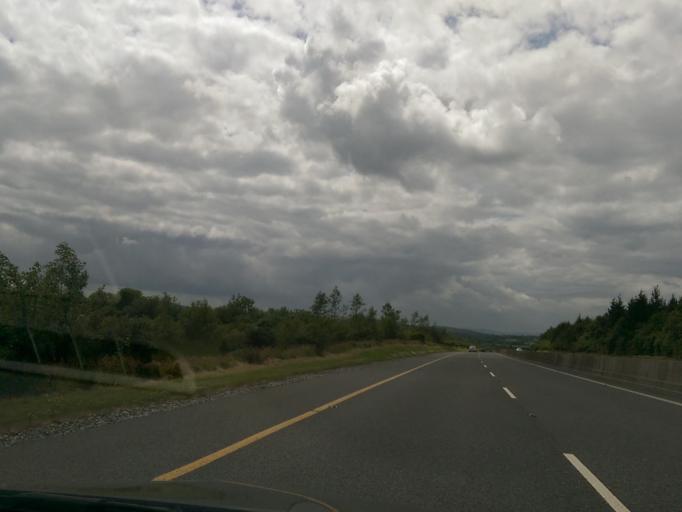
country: IE
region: Munster
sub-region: County Cork
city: Mitchelstown
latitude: 52.2749
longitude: -8.2333
